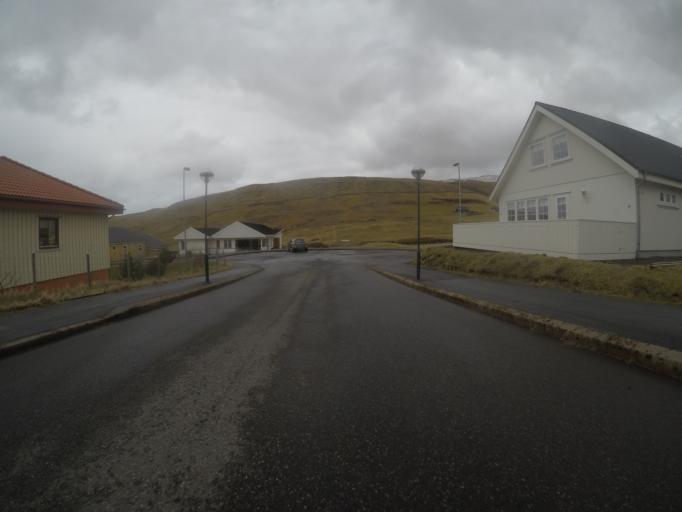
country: FO
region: Vagar
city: Midvagur
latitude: 62.0597
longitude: -7.1456
